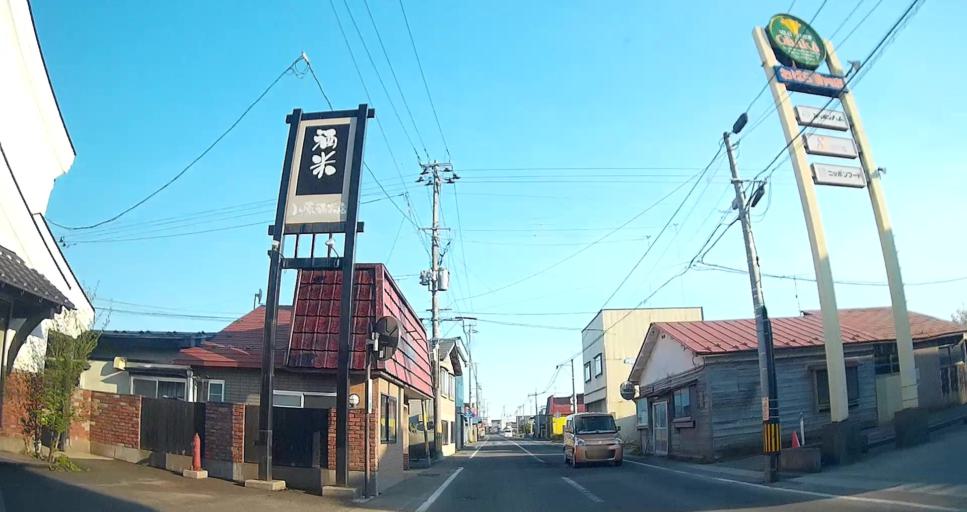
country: JP
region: Aomori
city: Mutsu
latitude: 41.2889
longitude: 141.2112
